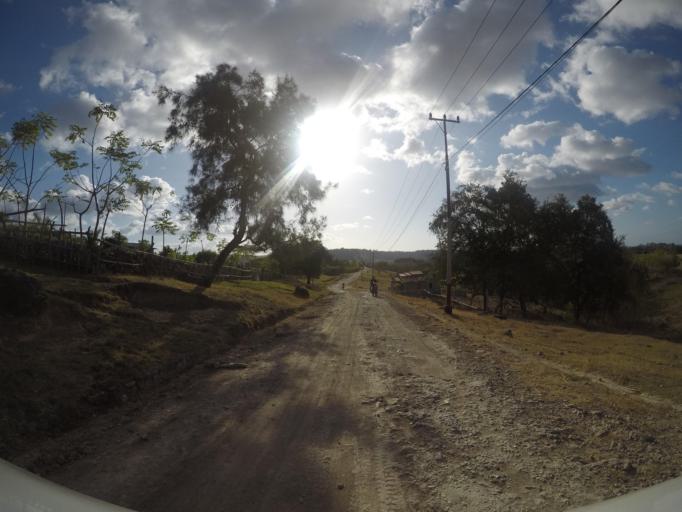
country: TL
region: Lautem
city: Lospalos
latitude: -8.4294
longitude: 126.8425
